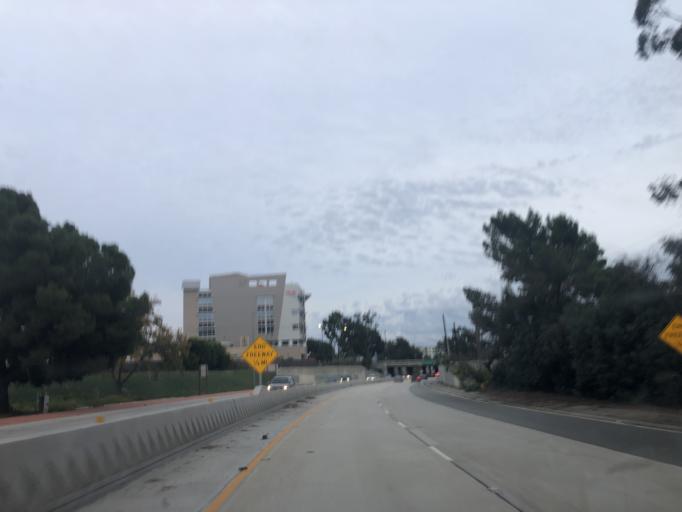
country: US
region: California
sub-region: Los Angeles County
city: Glendale
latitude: 34.1418
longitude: -118.2727
